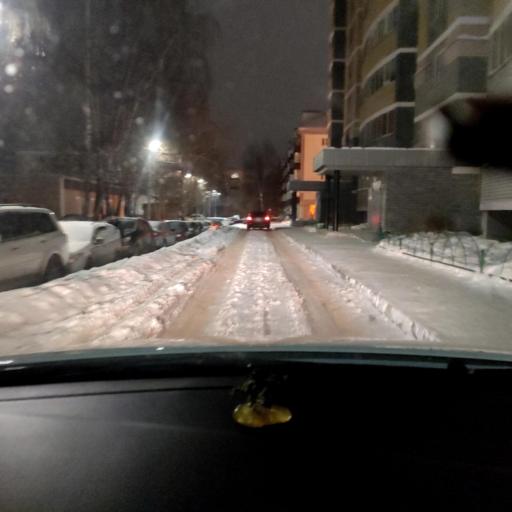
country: RU
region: Tatarstan
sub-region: Zelenodol'skiy Rayon
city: Zelenodolsk
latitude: 55.8555
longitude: 48.5007
